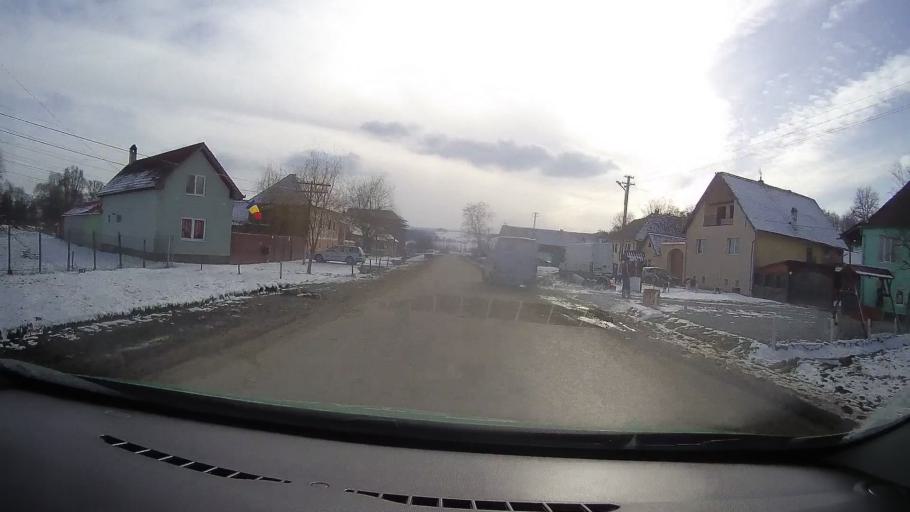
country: RO
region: Sibiu
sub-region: Comuna Bradeni
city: Bradeni
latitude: 46.0566
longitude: 24.7848
